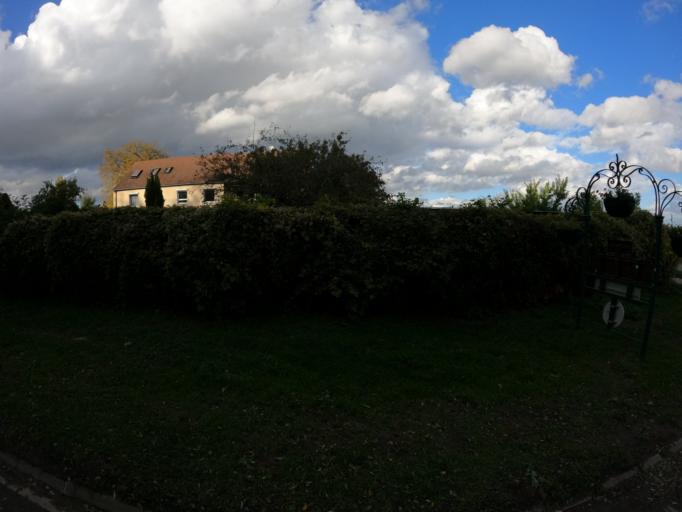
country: FR
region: Ile-de-France
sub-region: Departement de Seine-et-Marne
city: Chalifert
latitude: 48.8870
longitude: 2.7772
